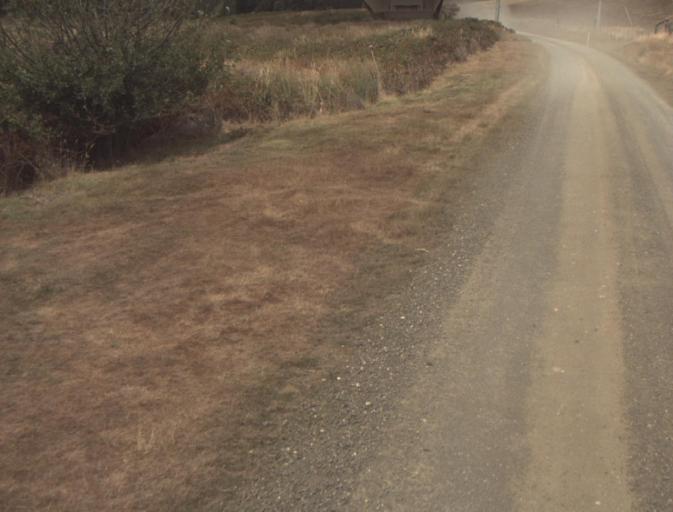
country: AU
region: Tasmania
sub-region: Dorset
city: Bridport
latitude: -41.1883
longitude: 147.2618
